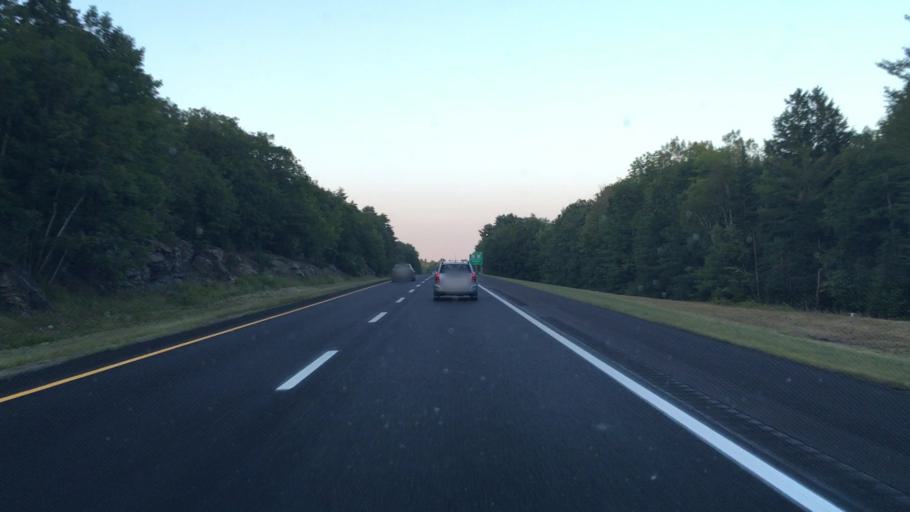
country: US
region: Maine
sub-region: Sagadahoc County
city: Topsham
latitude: 43.9987
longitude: -69.9316
